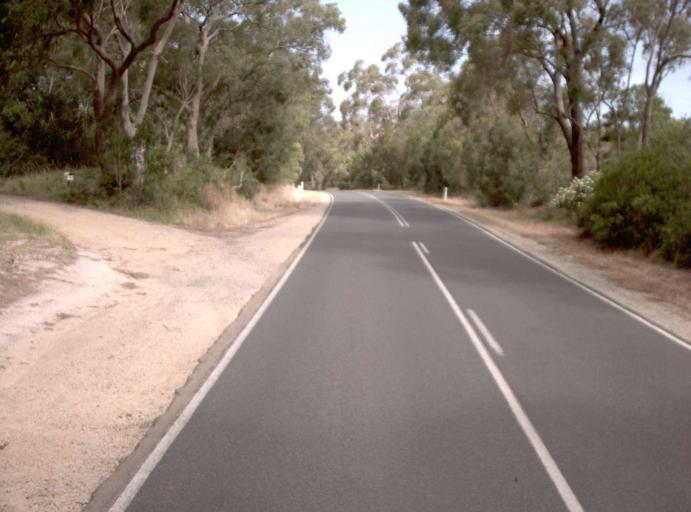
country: AU
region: Victoria
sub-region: Wellington
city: Sale
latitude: -38.2231
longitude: 147.1120
